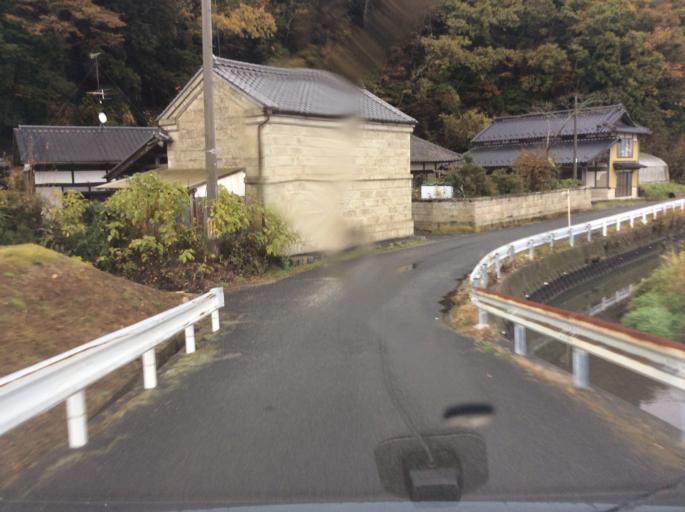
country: JP
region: Fukushima
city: Iwaki
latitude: 37.0884
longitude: 140.9548
